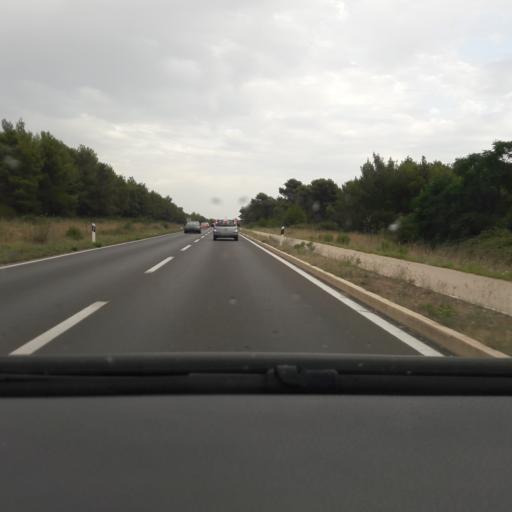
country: HR
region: Zadarska
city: Zadar
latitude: 44.1633
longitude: 15.2046
